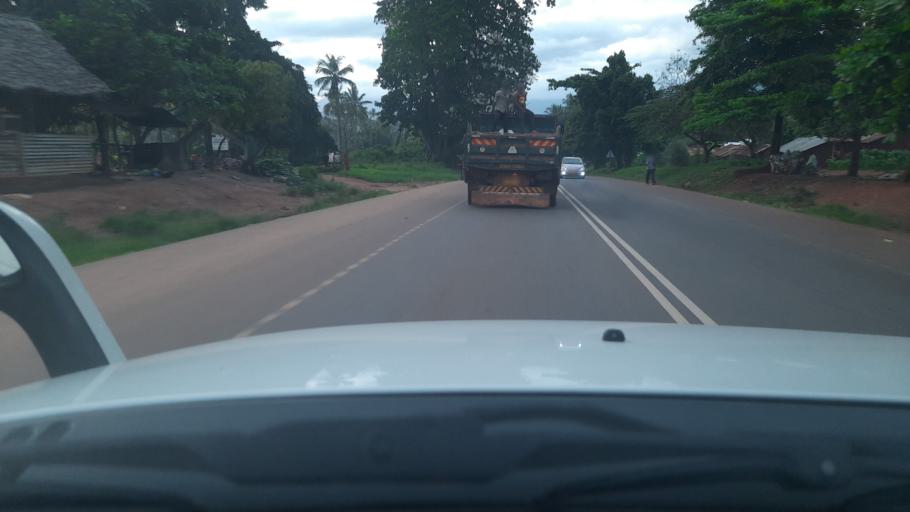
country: TZ
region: Tanga
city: Muheza
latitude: -5.1797
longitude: 38.8219
